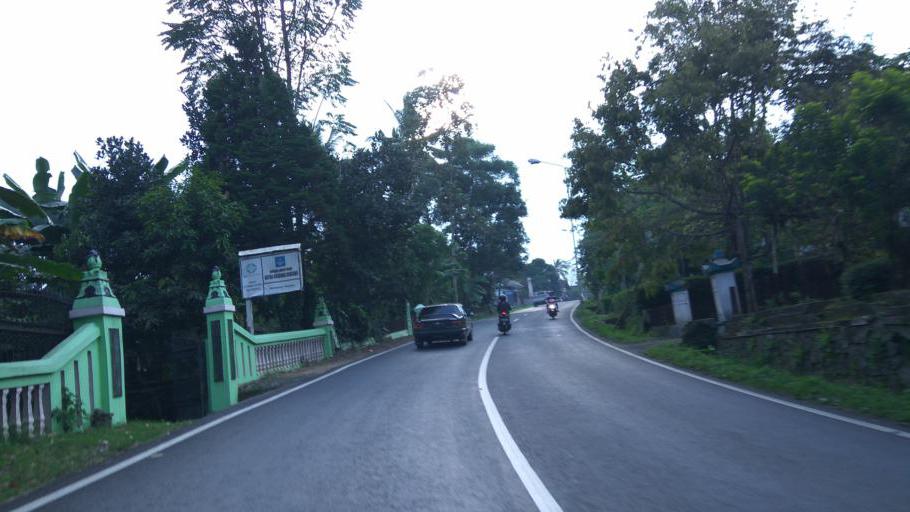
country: ID
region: Central Java
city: Salatiga
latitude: -7.3668
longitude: 110.4702
